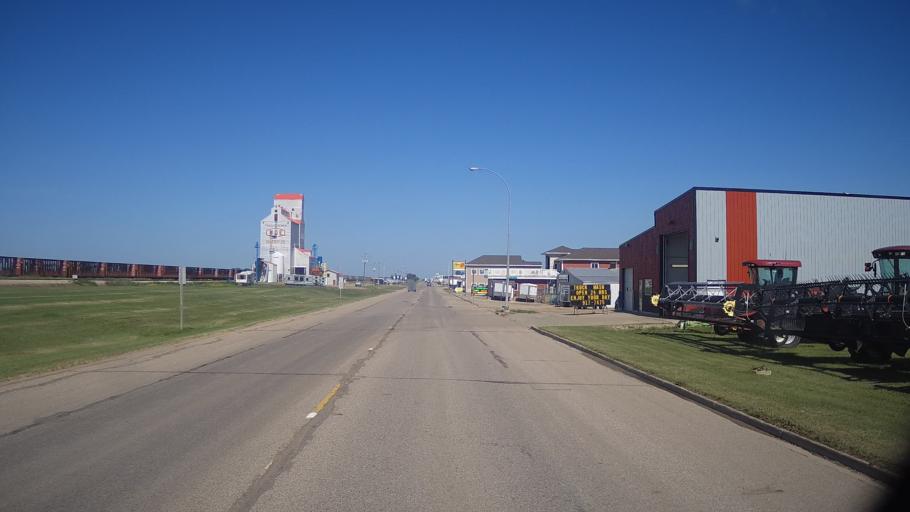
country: CA
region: Saskatchewan
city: Watrous
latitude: 51.6671
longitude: -105.4551
